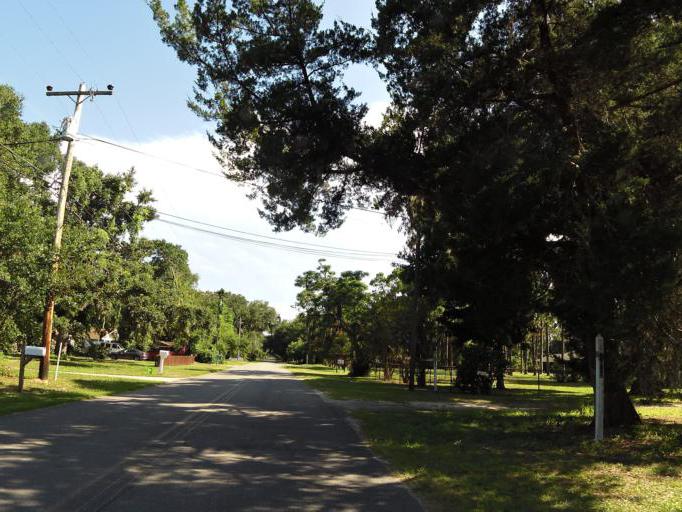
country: US
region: Florida
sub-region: Nassau County
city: Fernandina Beach
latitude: 30.6499
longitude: -81.4628
